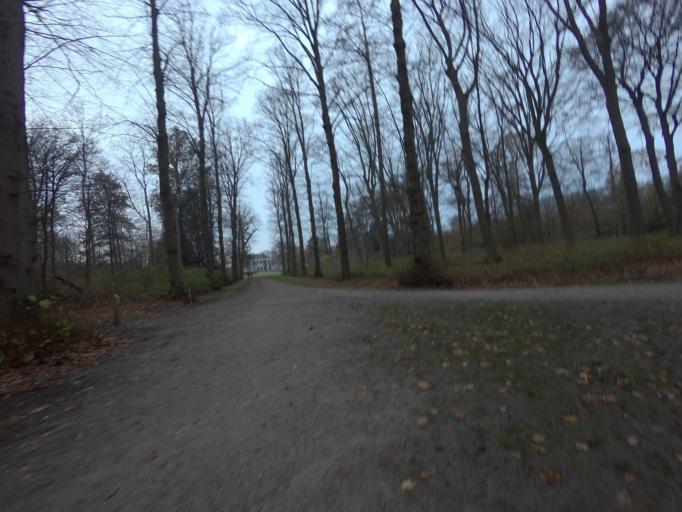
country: NL
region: North Holland
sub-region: Gemeente Wijdemeren
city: Kortenhoef
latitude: 52.2529
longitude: 5.1254
